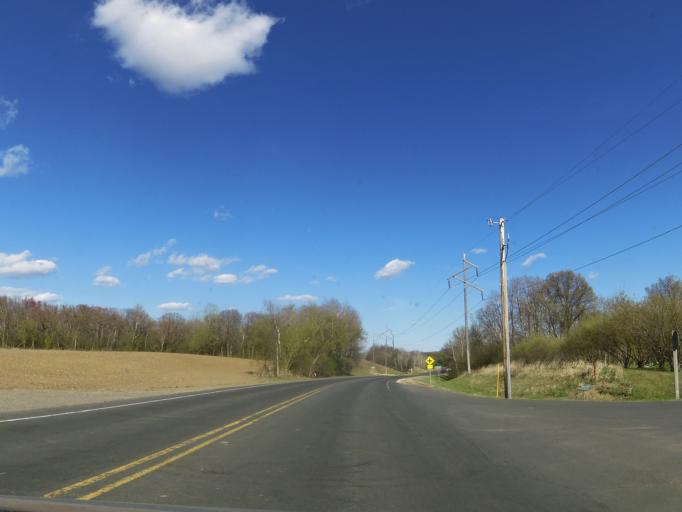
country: US
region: Wisconsin
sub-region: Saint Croix County
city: Somerset
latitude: 45.0355
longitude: -92.6726
